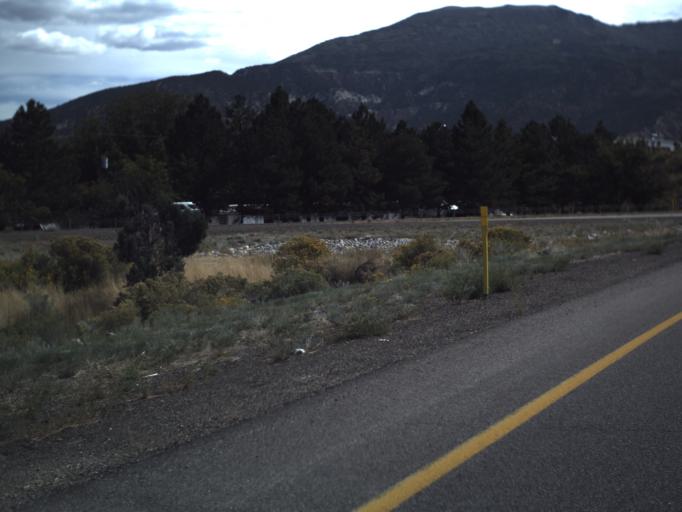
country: US
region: Utah
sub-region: Iron County
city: Cedar City
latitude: 37.6782
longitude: -113.0807
